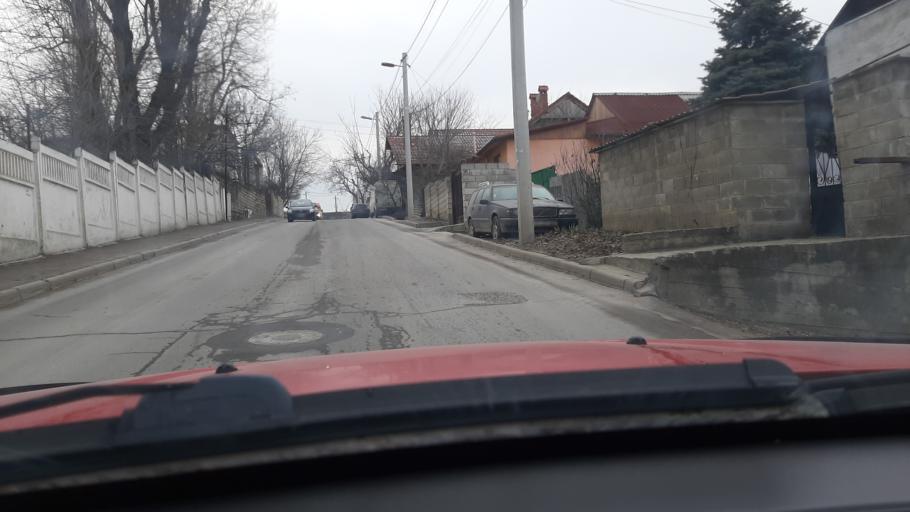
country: MD
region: Chisinau
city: Vatra
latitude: 47.0379
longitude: 28.7921
